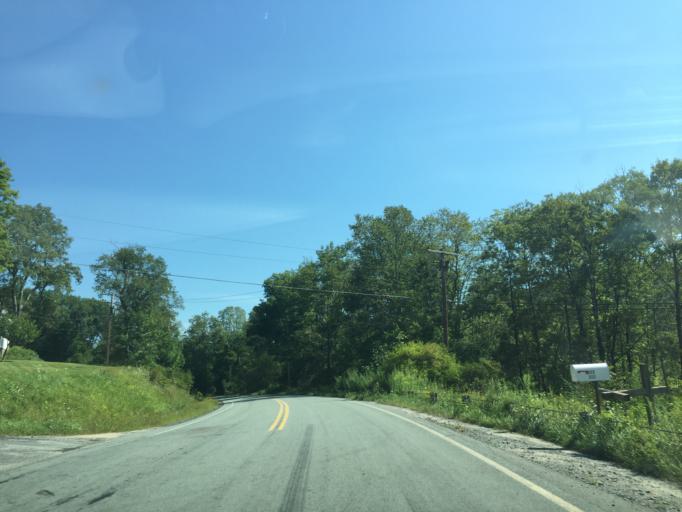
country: US
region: New York
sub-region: Sullivan County
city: Livingston Manor
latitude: 41.8036
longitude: -74.9733
